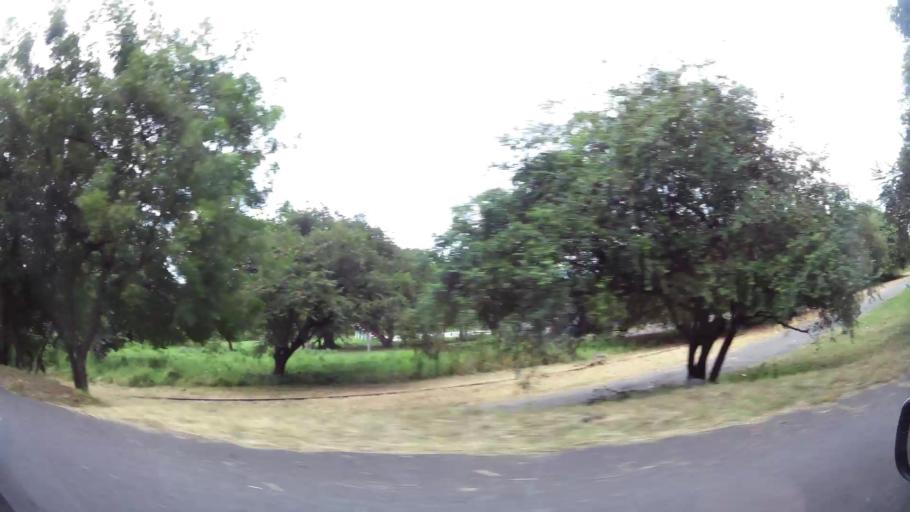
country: CR
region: Puntarenas
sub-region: Canton Central de Puntarenas
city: Chacarita
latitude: 9.9779
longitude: -84.7389
